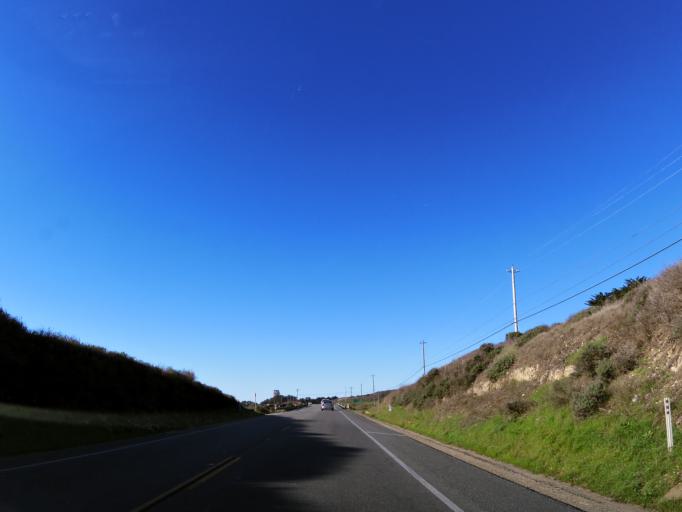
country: US
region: California
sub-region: Santa Cruz County
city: Bonny Doon
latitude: 37.0043
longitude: -122.1839
